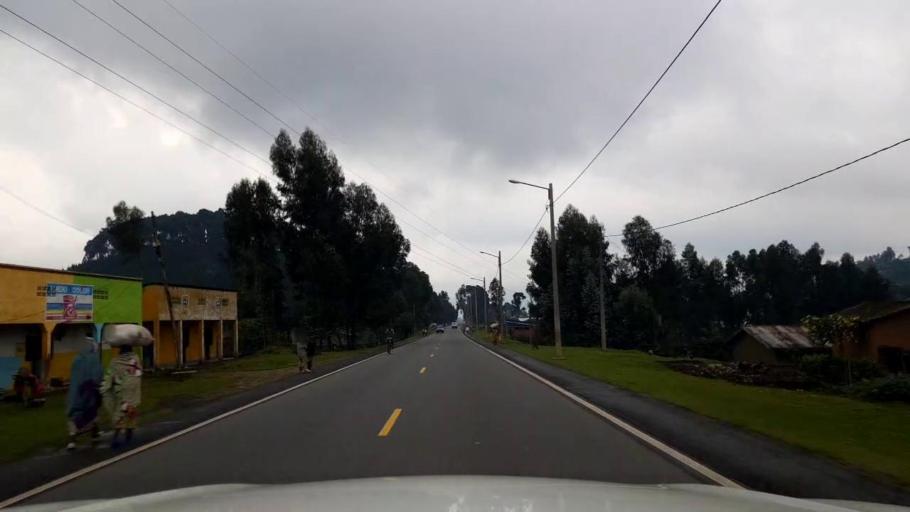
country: RW
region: Northern Province
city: Musanze
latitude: -1.5417
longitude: 29.5599
